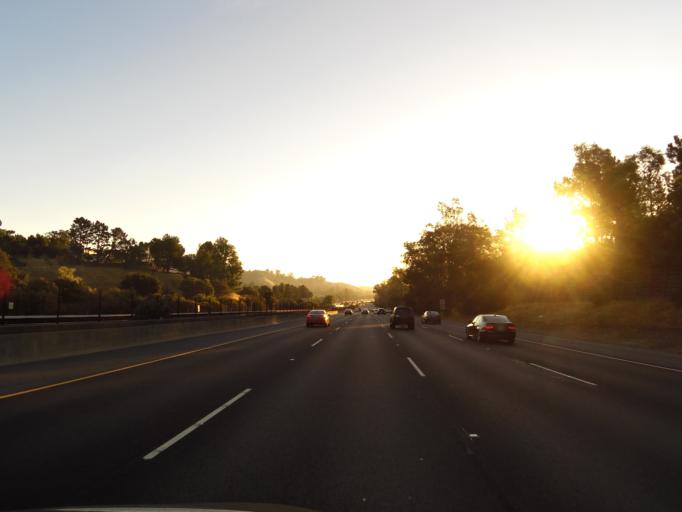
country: US
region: California
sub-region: Contra Costa County
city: Lafayette
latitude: 37.8909
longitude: -122.1329
